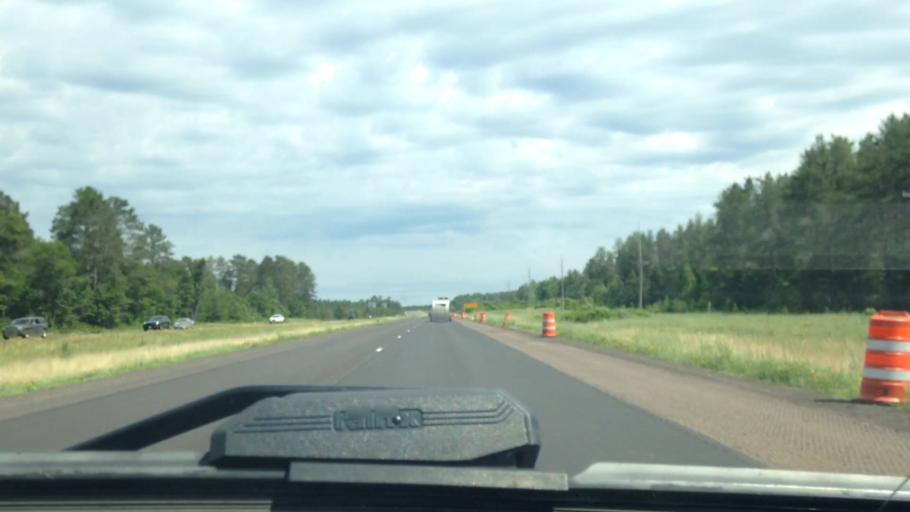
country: US
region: Wisconsin
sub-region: Washburn County
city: Spooner
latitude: 46.1603
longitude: -91.8087
